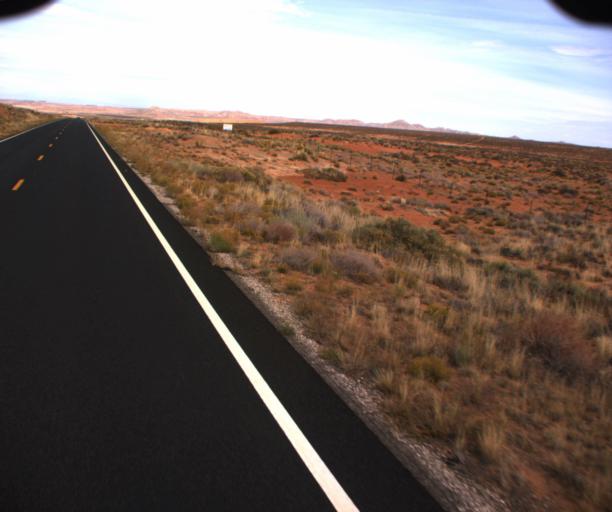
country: US
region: Arizona
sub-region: Apache County
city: Many Farms
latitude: 36.8884
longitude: -109.6273
